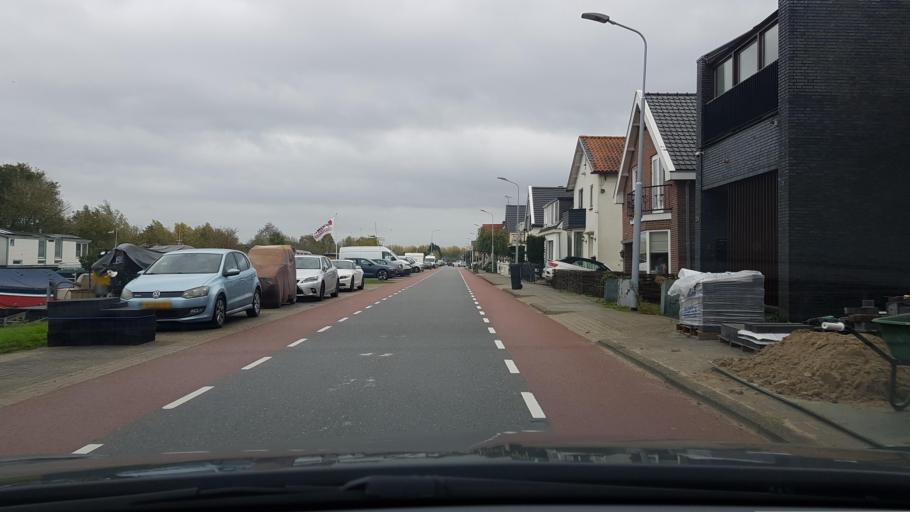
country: NL
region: North Holland
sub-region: Gemeente Aalsmeer
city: Aalsmeer
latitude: 52.3440
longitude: 4.7845
